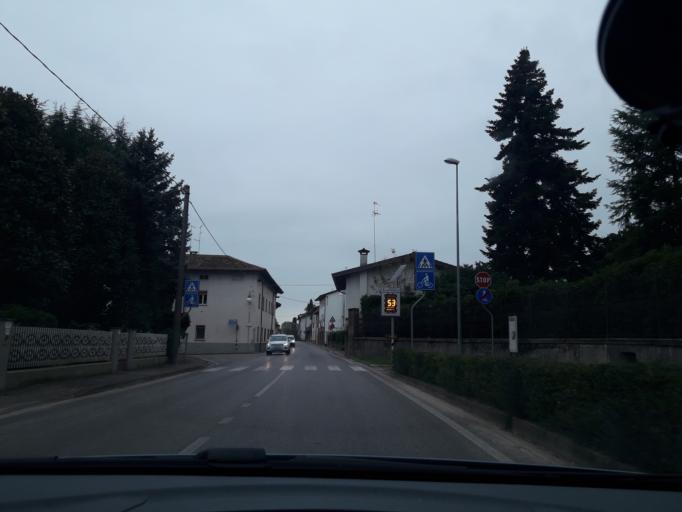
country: IT
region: Friuli Venezia Giulia
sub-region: Provincia di Udine
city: Martignacco
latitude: 46.0984
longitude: 13.1379
